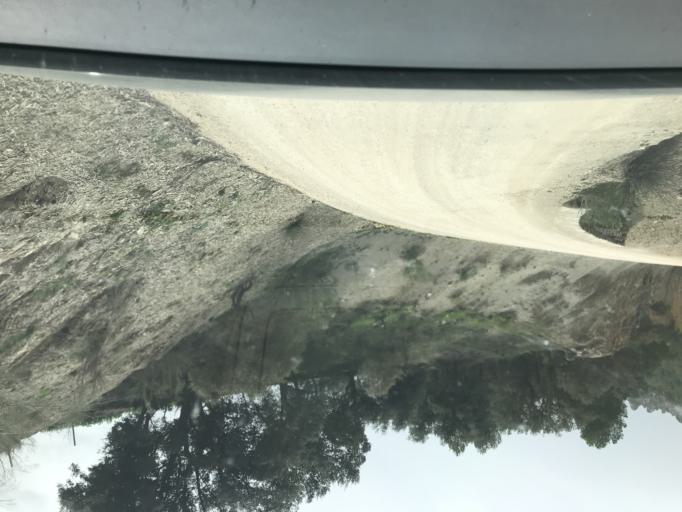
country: ES
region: Andalusia
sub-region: Provincia de Granada
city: Castril
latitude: 37.8471
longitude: -2.7746
